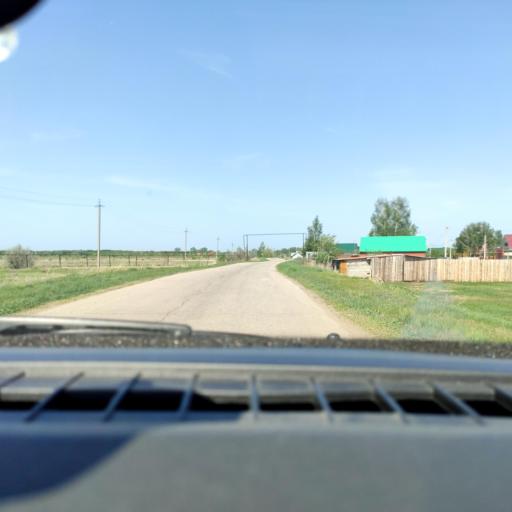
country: RU
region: Samara
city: Georgiyevka
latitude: 53.2690
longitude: 50.9596
